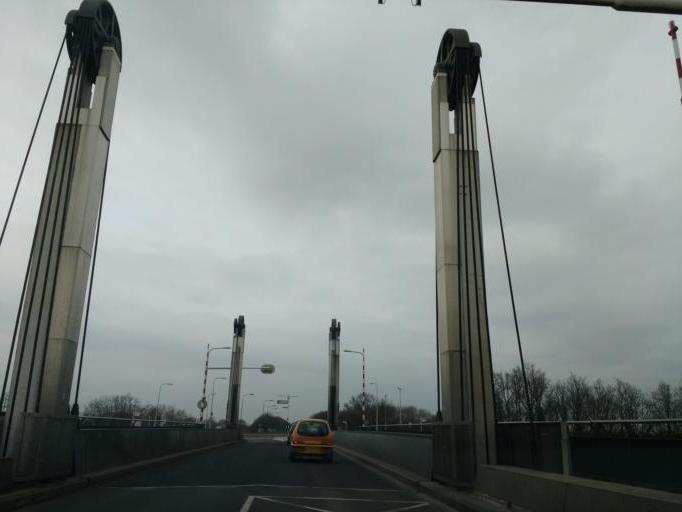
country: NL
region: Gelderland
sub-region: Gemeente Overbetuwe
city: Oosterhout
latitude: 51.8548
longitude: 5.8229
